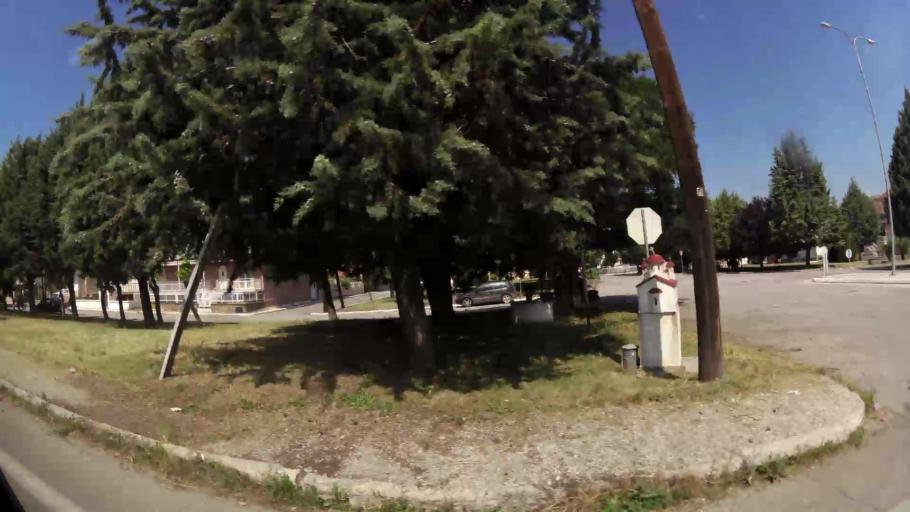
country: GR
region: West Macedonia
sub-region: Nomos Kozanis
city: Koila
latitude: 40.3355
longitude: 21.7916
